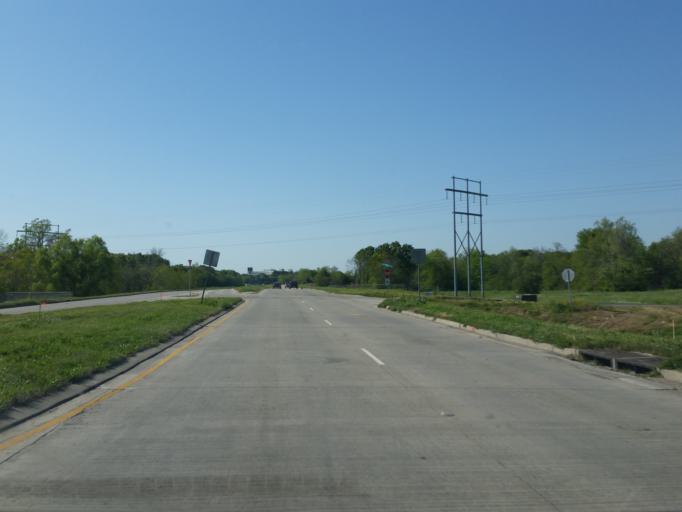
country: US
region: Louisiana
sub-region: Lafayette Parish
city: Youngsville
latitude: 30.1404
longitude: -92.0239
